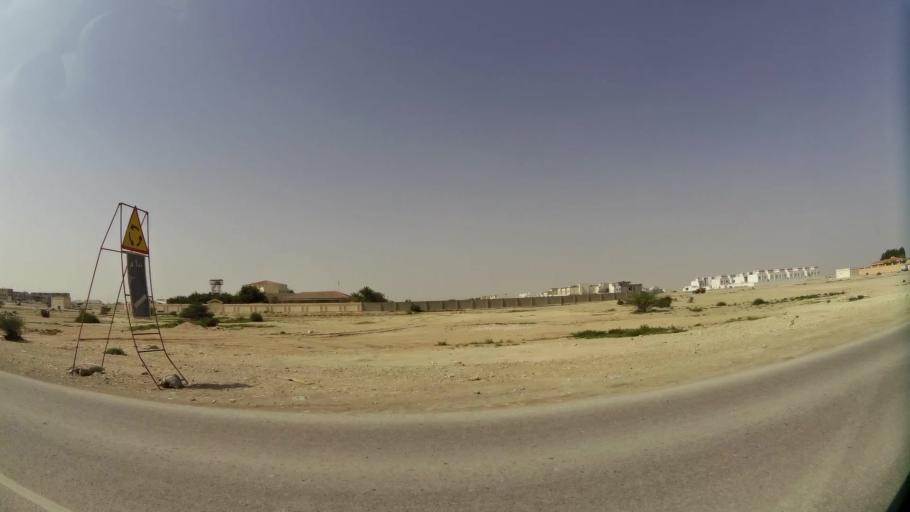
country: QA
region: Baladiyat Umm Salal
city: Umm Salal Muhammad
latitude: 25.4138
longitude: 51.4309
